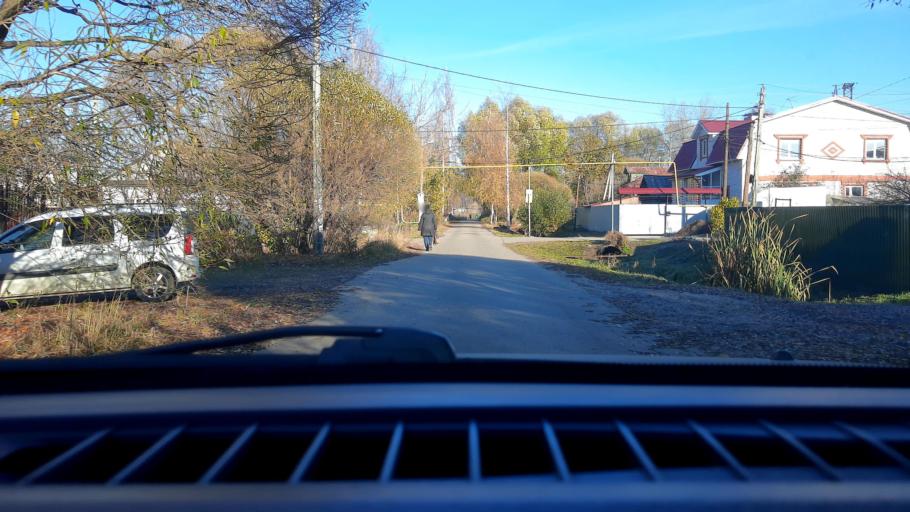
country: RU
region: Nizjnij Novgorod
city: Nizhniy Novgorod
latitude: 56.2905
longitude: 43.8982
